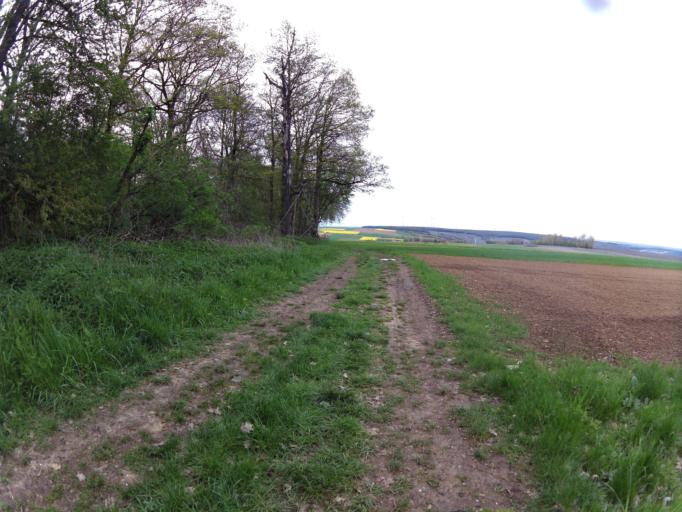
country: DE
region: Bavaria
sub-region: Regierungsbezirk Unterfranken
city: Prosselsheim
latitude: 49.8592
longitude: 10.1564
